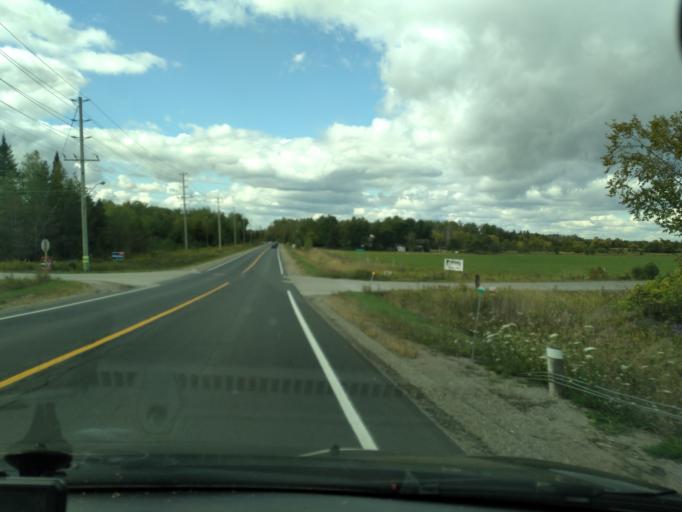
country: CA
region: Ontario
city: Angus
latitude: 44.2577
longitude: -79.7839
